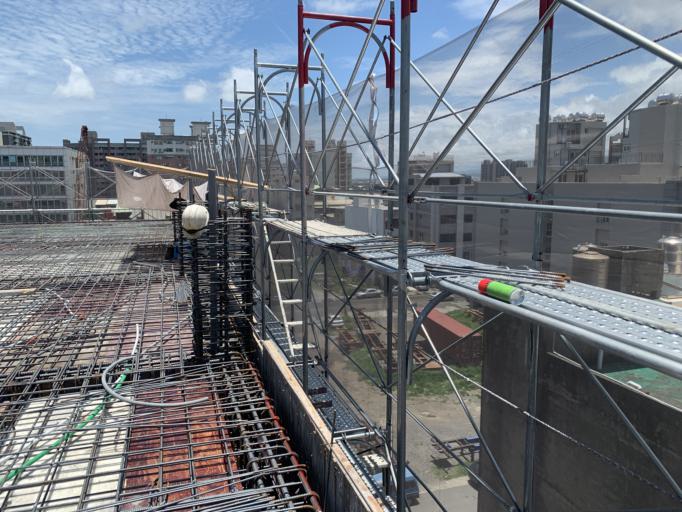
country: TW
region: Taiwan
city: Fengyuan
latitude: 24.2612
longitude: 120.5326
